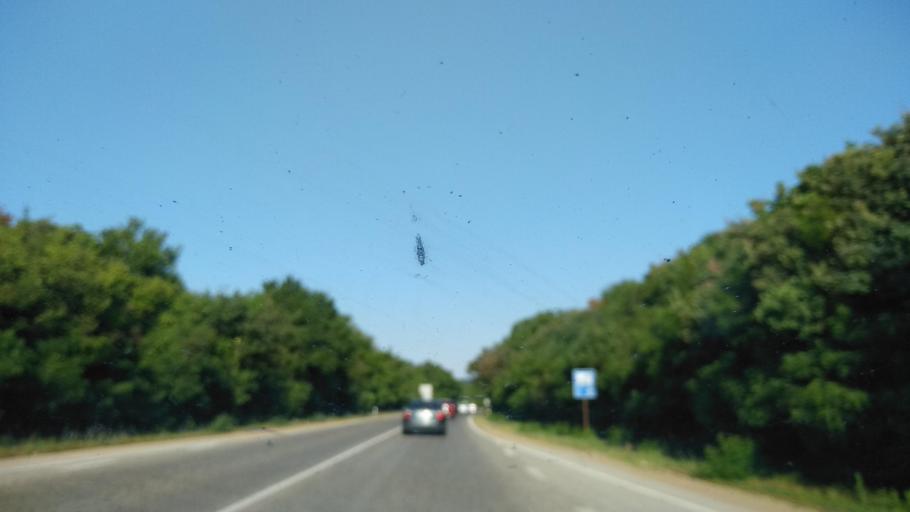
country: BG
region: Lovech
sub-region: Obshtina Lovech
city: Lovech
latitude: 43.0460
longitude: 24.8803
